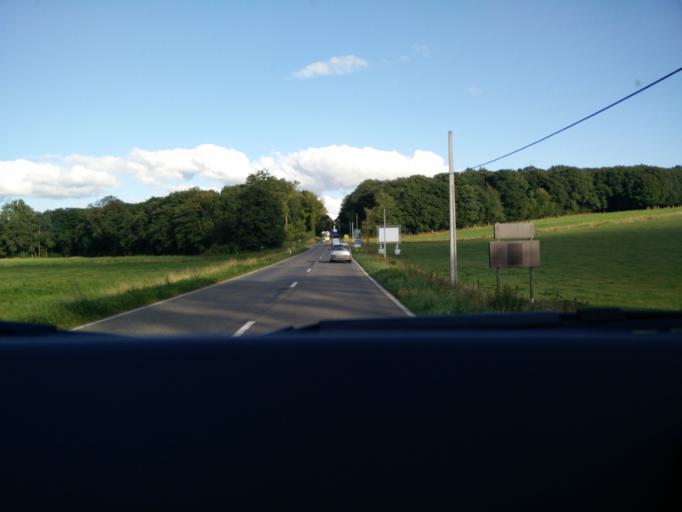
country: BE
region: Wallonia
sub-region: Province de Namur
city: Walcourt
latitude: 50.2060
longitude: 4.4792
